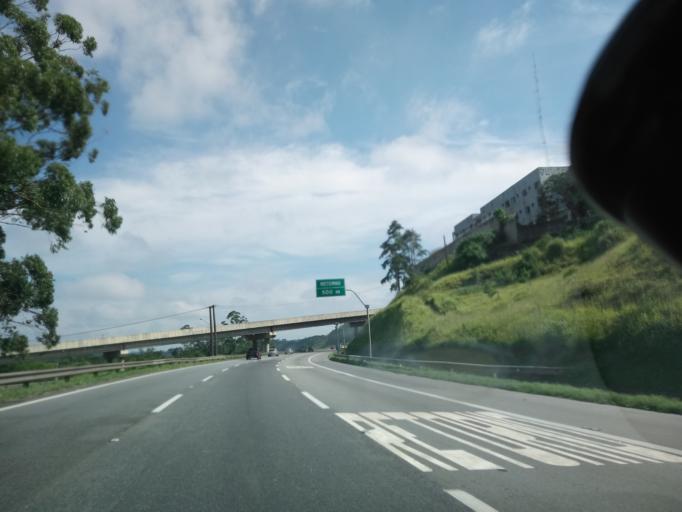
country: BR
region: Sao Paulo
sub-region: Itapecerica Da Serra
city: Itapecerica da Serra
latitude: -23.6935
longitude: -46.8184
